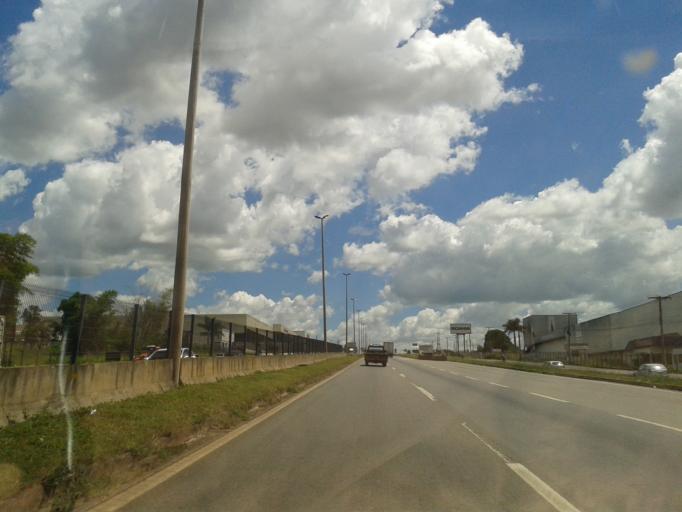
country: BR
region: Goias
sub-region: Aparecida De Goiania
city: Aparecida de Goiania
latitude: -16.7832
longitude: -49.2373
